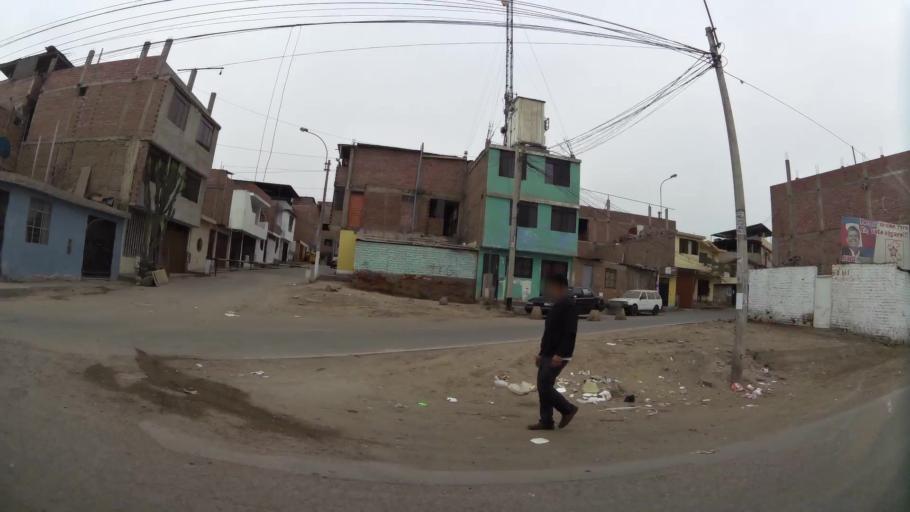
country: PE
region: Lima
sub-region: Lima
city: Surco
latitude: -12.1766
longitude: -76.9703
